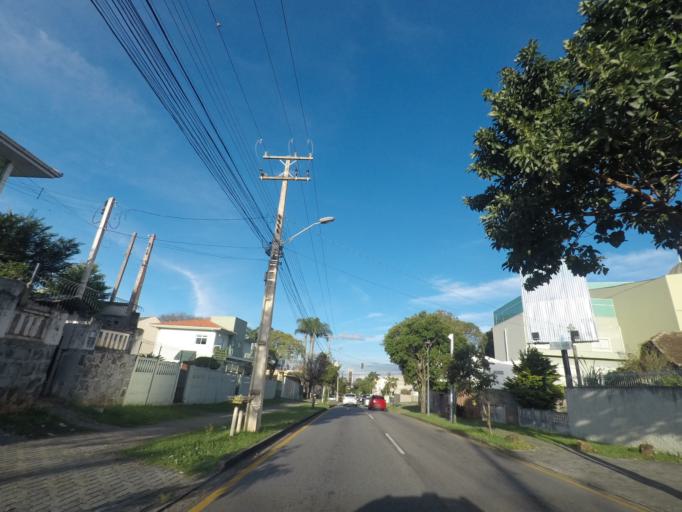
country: BR
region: Parana
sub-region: Curitiba
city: Curitiba
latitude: -25.4169
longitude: -49.2774
